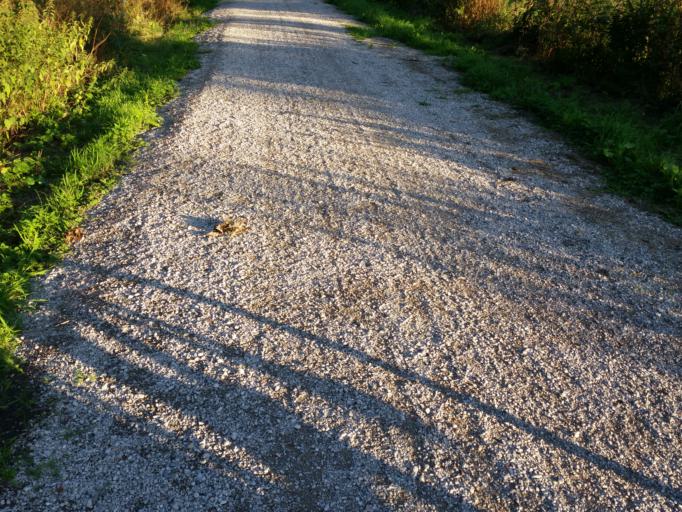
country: NL
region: North Holland
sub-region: Gemeente Amsterdam
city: Driemond
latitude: 52.3222
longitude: 4.9996
